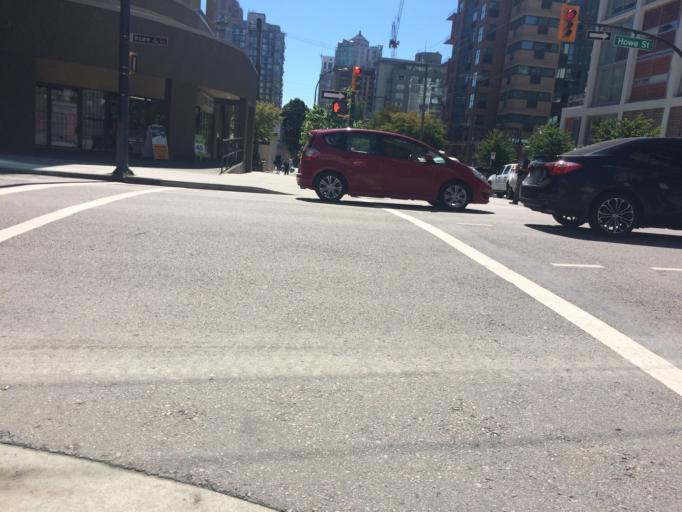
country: CA
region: British Columbia
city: West End
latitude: 49.2768
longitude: -123.1288
